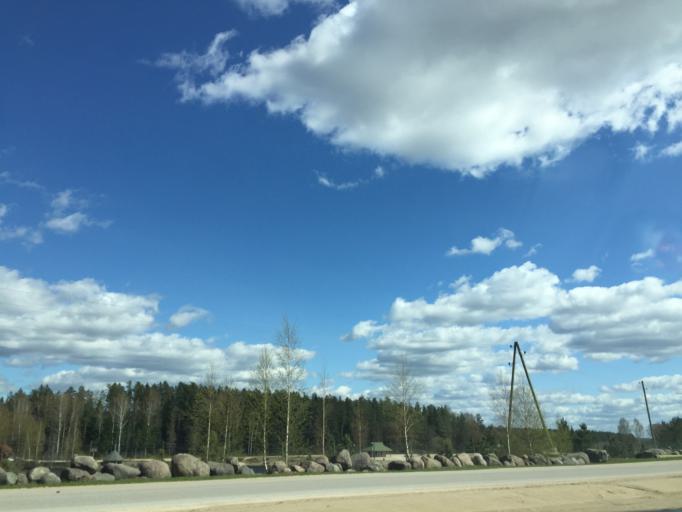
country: LV
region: Vilanu
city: Vilani
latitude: 56.5747
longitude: 27.0433
